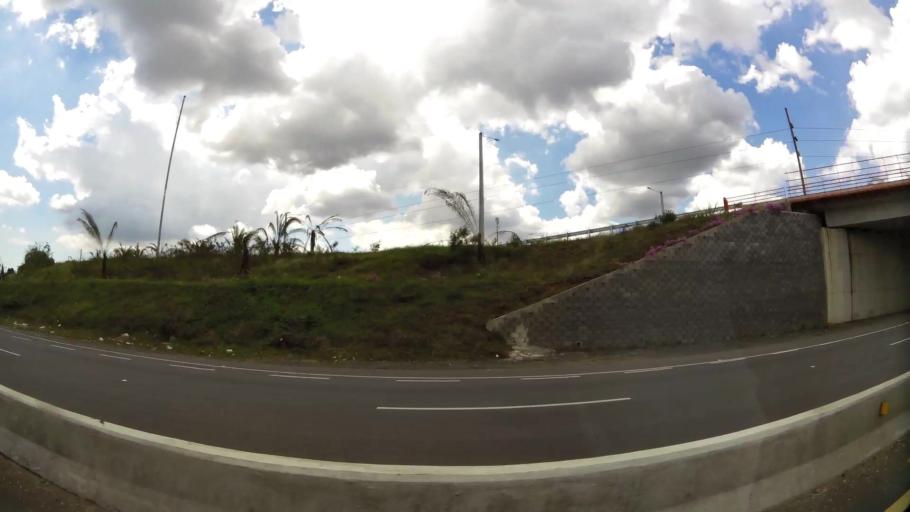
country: DO
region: Nacional
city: Santo Domingo
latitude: 18.5671
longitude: -69.9796
